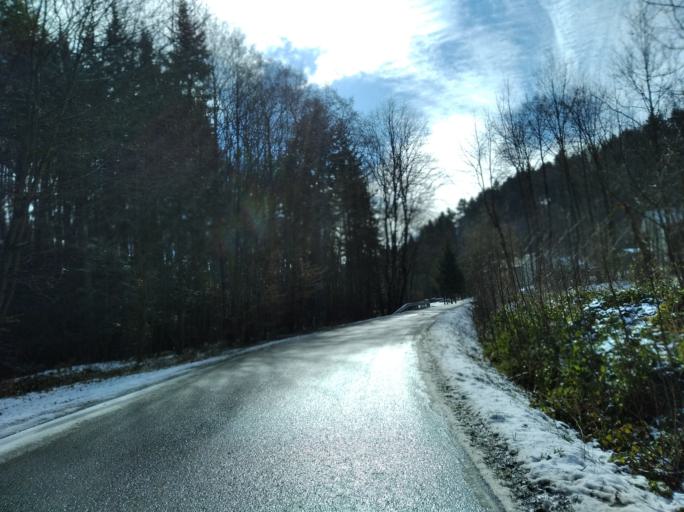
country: PL
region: Subcarpathian Voivodeship
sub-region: Powiat brzozowski
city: Jablonica Polska
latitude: 49.7481
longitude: 21.8807
